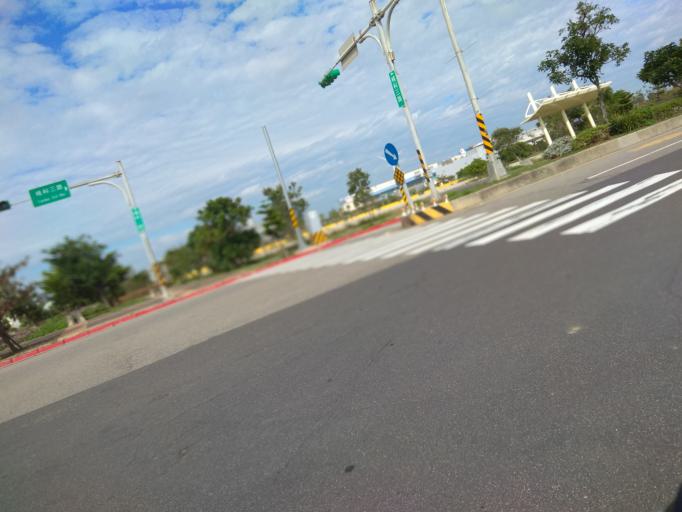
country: TW
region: Taiwan
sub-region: Hsinchu
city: Zhubei
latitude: 25.0346
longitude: 121.0715
